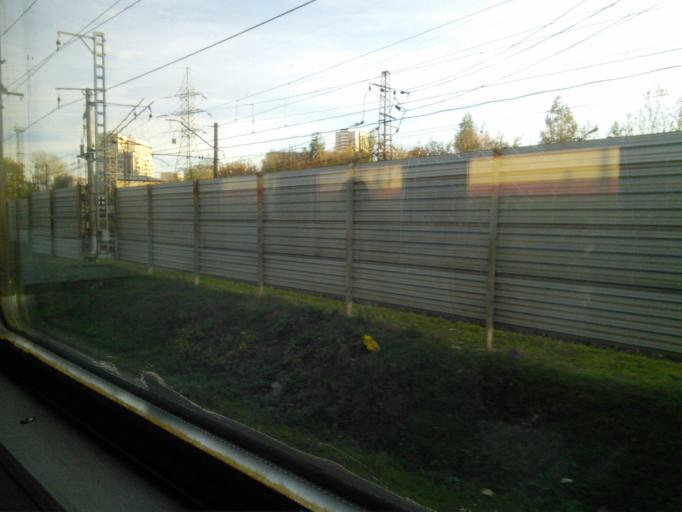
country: RU
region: Moscow
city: Mar'ina Roshcha
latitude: 55.8119
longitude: 37.6119
